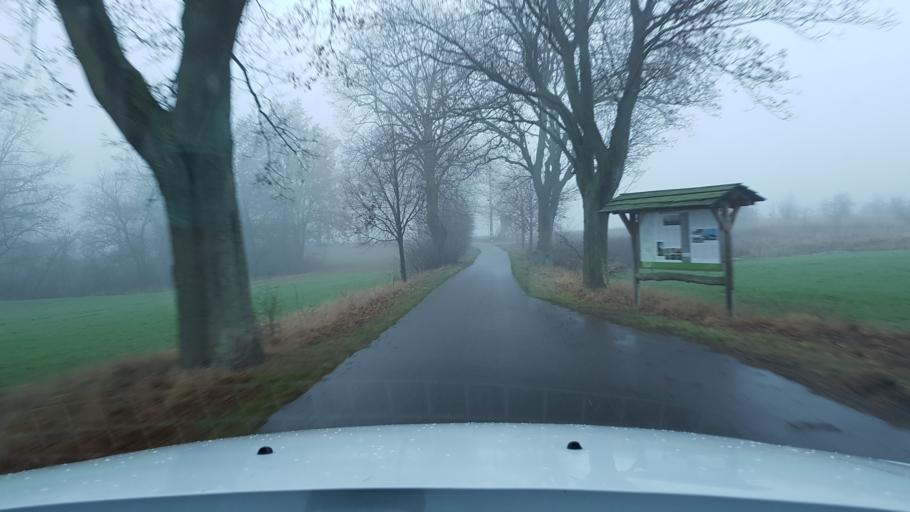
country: DE
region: Brandenburg
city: Mescherin
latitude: 53.2755
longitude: 14.4228
